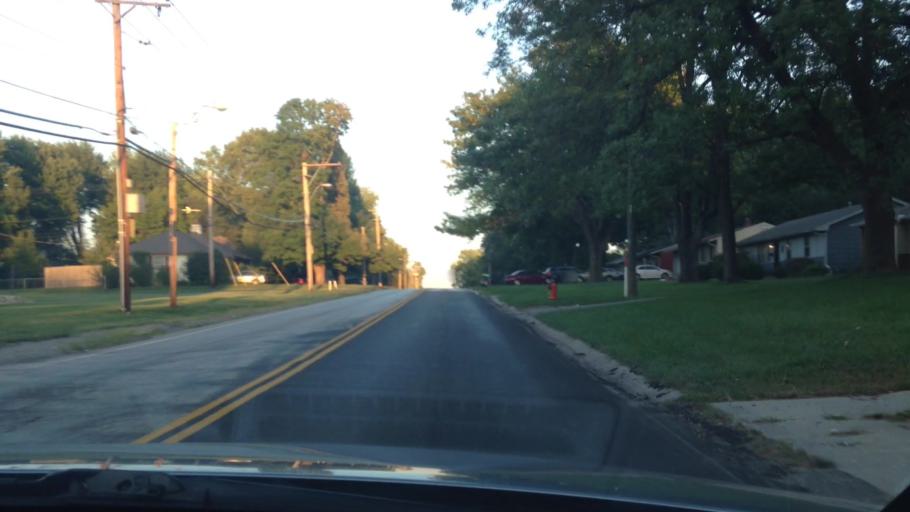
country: US
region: Missouri
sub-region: Jackson County
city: Grandview
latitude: 38.9241
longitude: -94.5383
